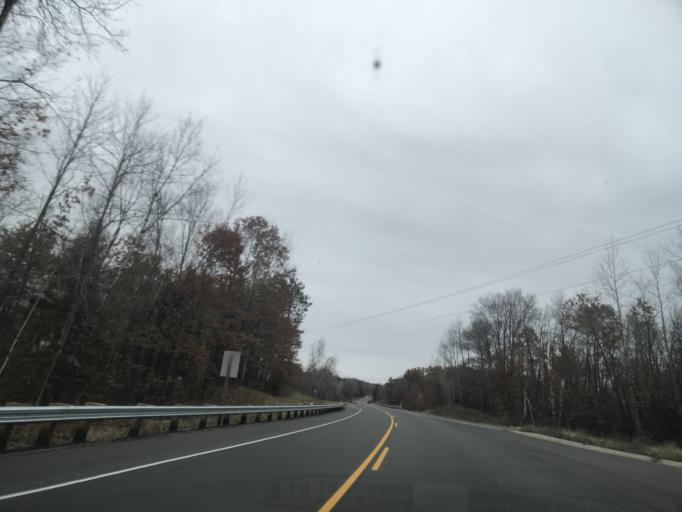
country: US
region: Wisconsin
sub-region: Menominee County
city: Legend Lake
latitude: 45.2725
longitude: -88.5086
